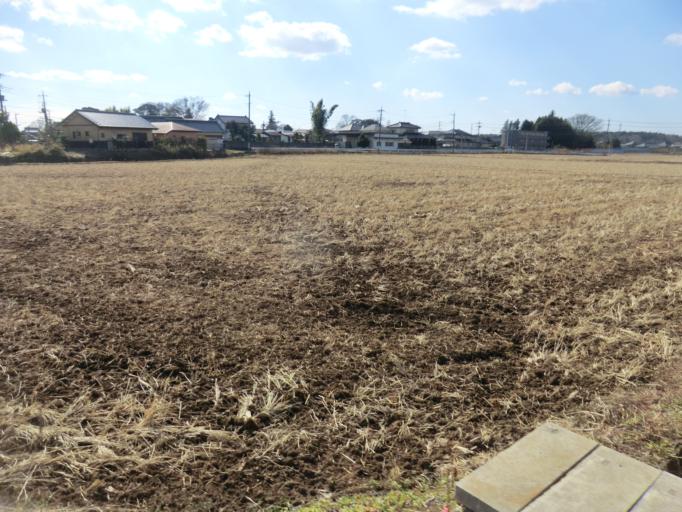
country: JP
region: Ibaraki
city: Naka
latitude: 36.1094
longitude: 140.1448
